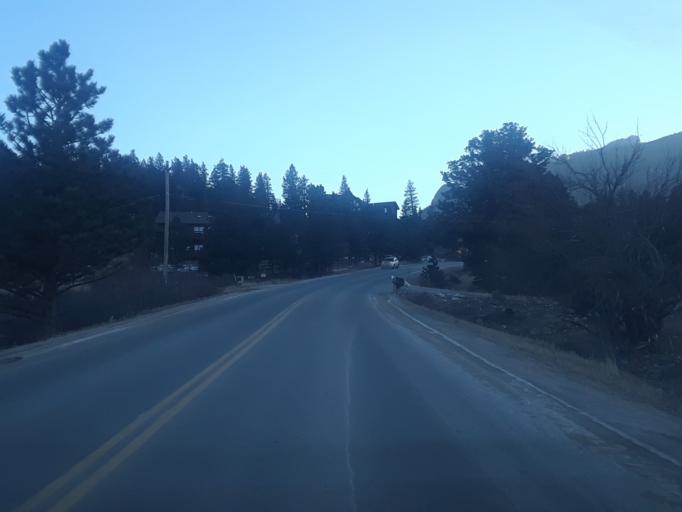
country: US
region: Colorado
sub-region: Larimer County
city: Estes Park
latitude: 40.3550
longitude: -105.5419
